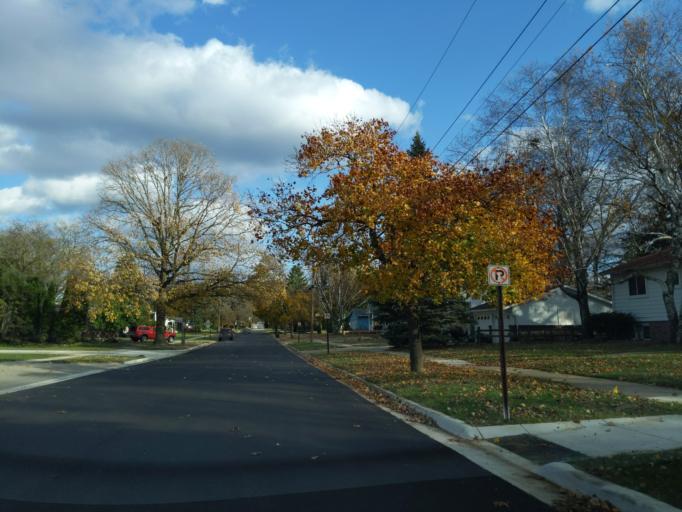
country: US
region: Michigan
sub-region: Ingham County
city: East Lansing
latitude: 42.7483
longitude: -84.5140
